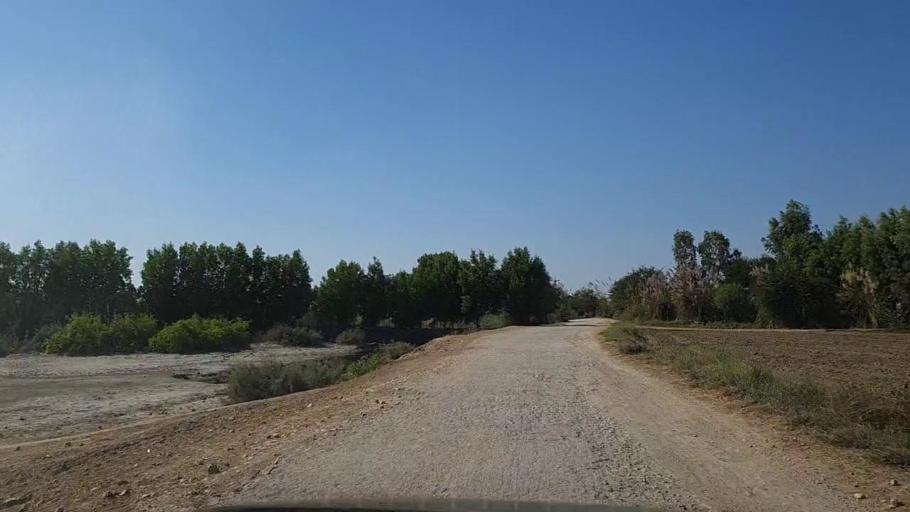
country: PK
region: Sindh
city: Mirpur Sakro
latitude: 24.6127
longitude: 67.7779
